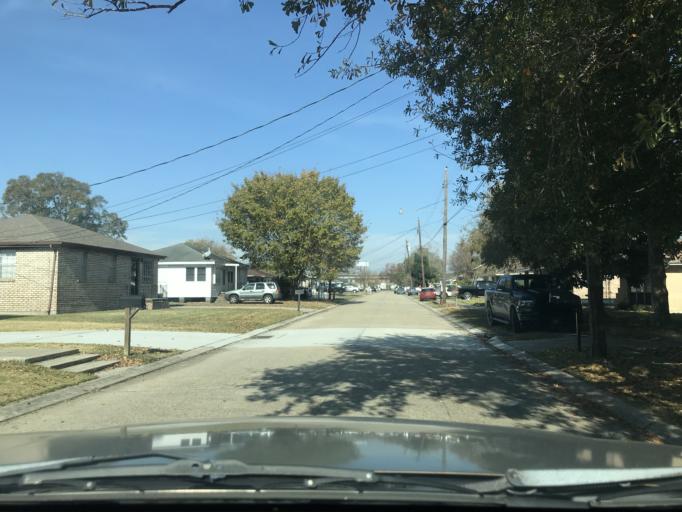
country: US
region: Louisiana
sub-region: Jefferson Parish
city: Marrero
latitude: 29.8928
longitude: -90.0901
